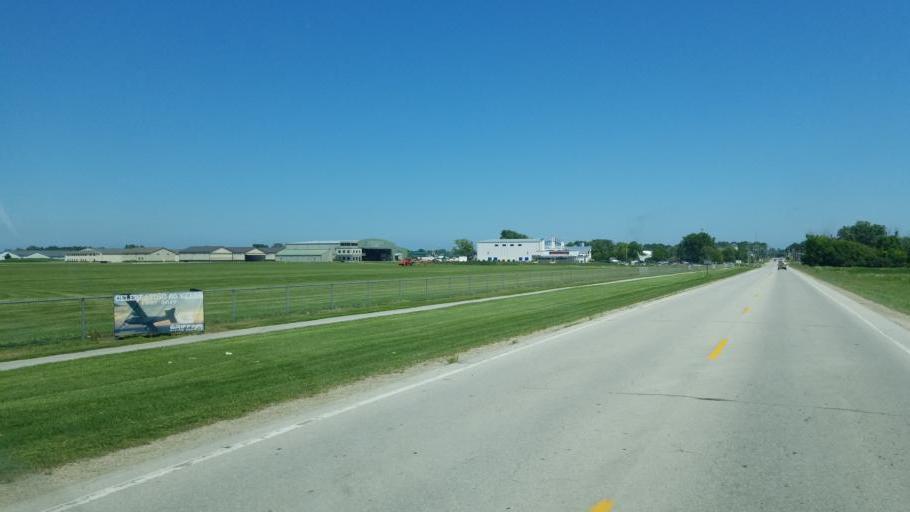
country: US
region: Ohio
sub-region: Ottawa County
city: Port Clinton
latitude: 41.5083
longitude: -82.8686
